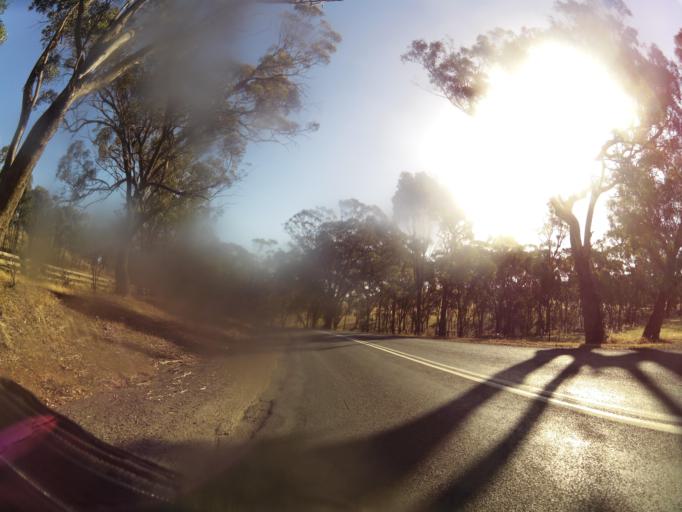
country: AU
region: Victoria
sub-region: Murrindindi
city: Kinglake West
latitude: -37.0122
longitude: 145.1190
